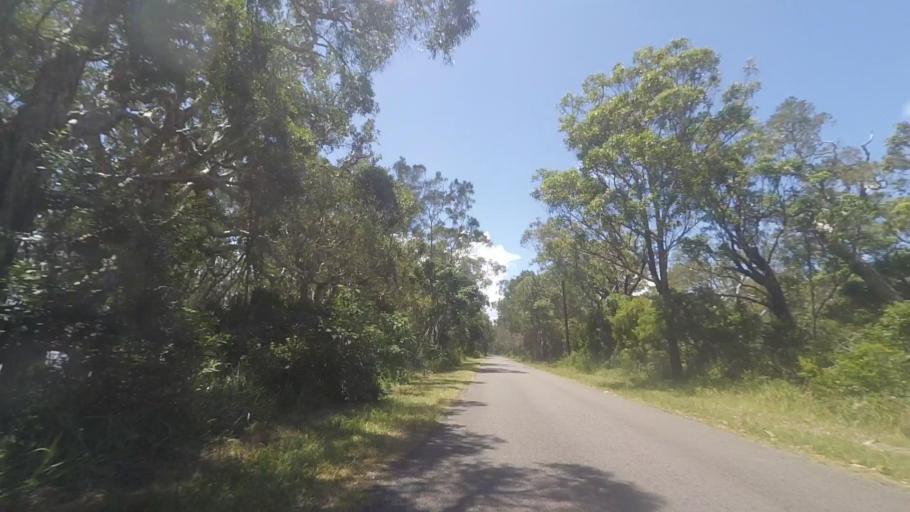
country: AU
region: New South Wales
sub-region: Great Lakes
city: Bulahdelah
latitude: -32.5325
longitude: 152.3215
